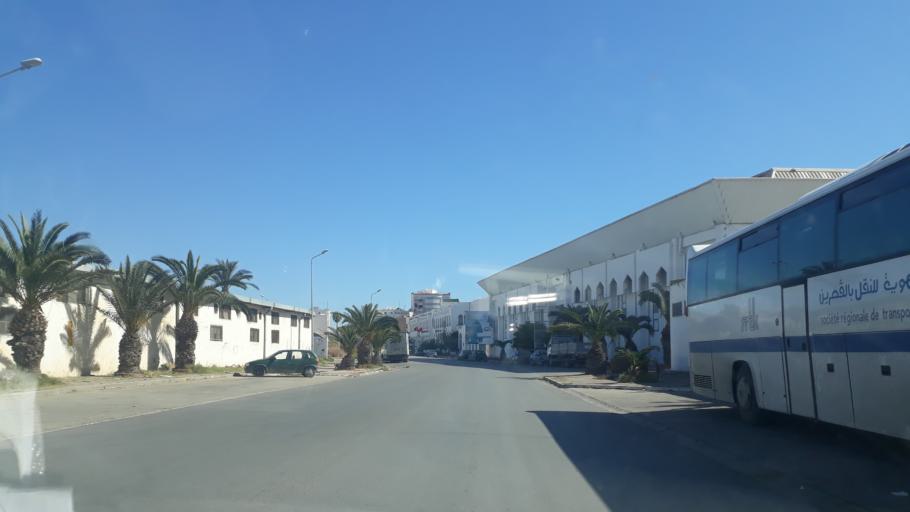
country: TN
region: Safaqis
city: Sfax
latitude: 34.7273
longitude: 10.7570
